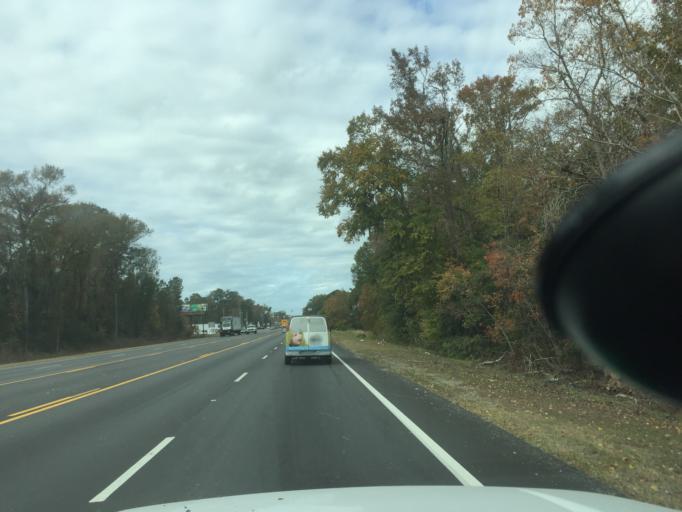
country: US
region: Georgia
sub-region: Chatham County
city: Garden City
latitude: 32.0920
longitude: -81.1935
